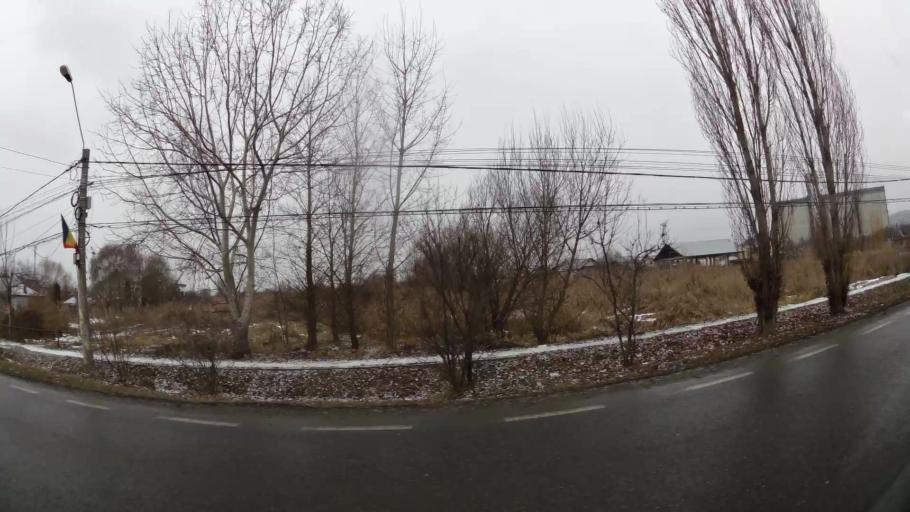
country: RO
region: Dambovita
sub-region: Comuna Aninoasa
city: Viforata
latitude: 44.9450
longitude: 25.4649
